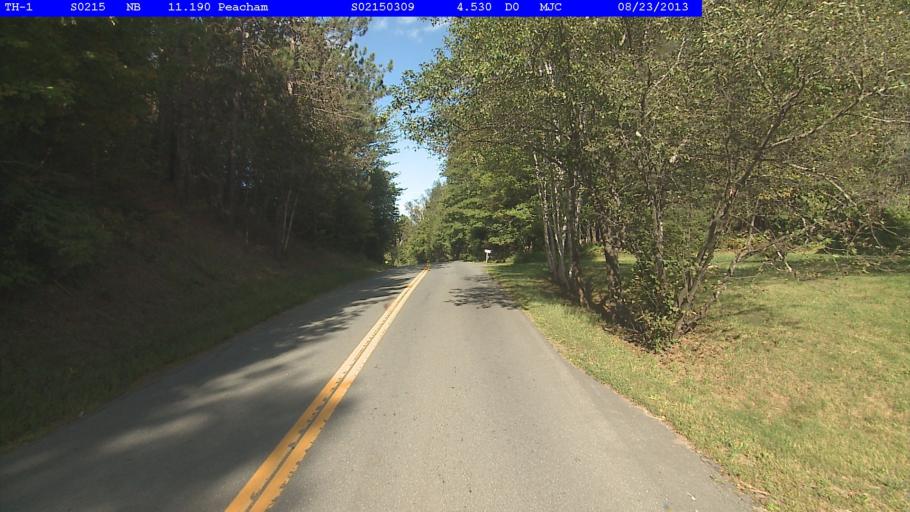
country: US
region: Vermont
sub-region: Caledonia County
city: Saint Johnsbury
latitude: 44.3600
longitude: -72.1715
